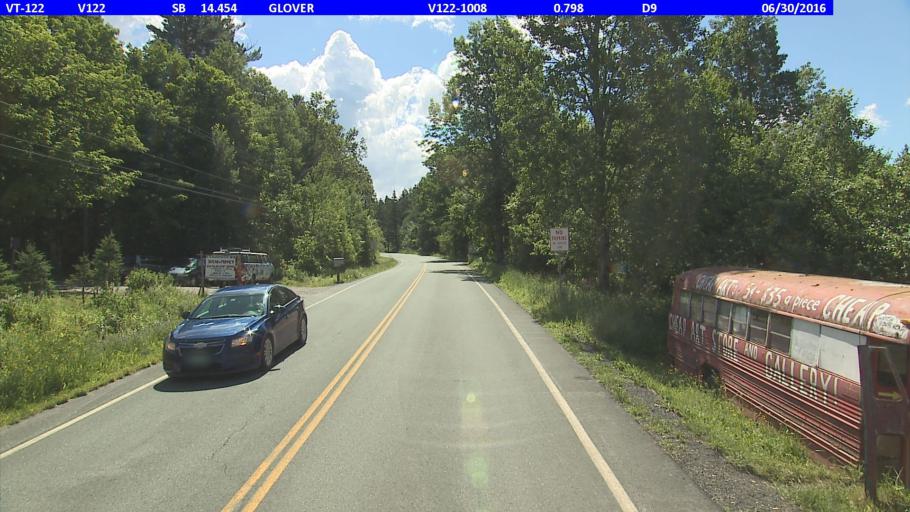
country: US
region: Vermont
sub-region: Caledonia County
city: Lyndonville
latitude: 44.6840
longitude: -72.1780
